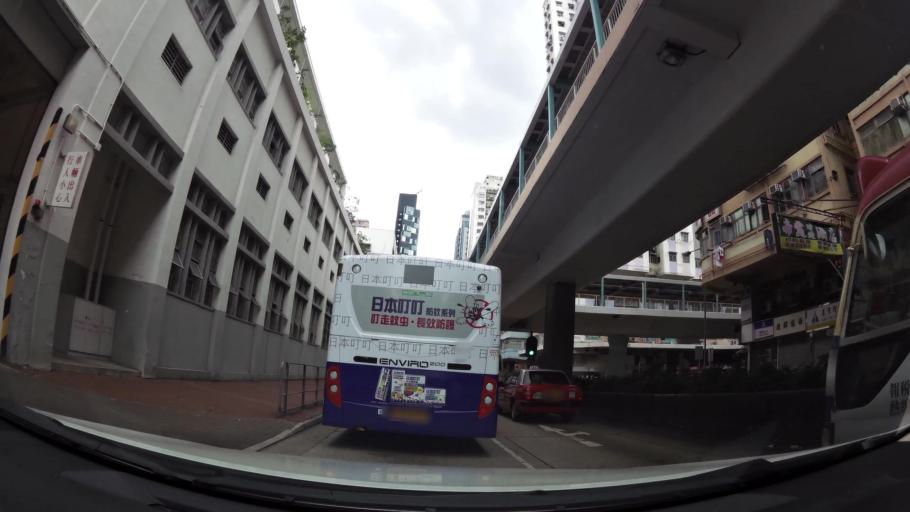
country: HK
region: Kowloon City
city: Kowloon
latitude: 22.3215
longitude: 114.1713
